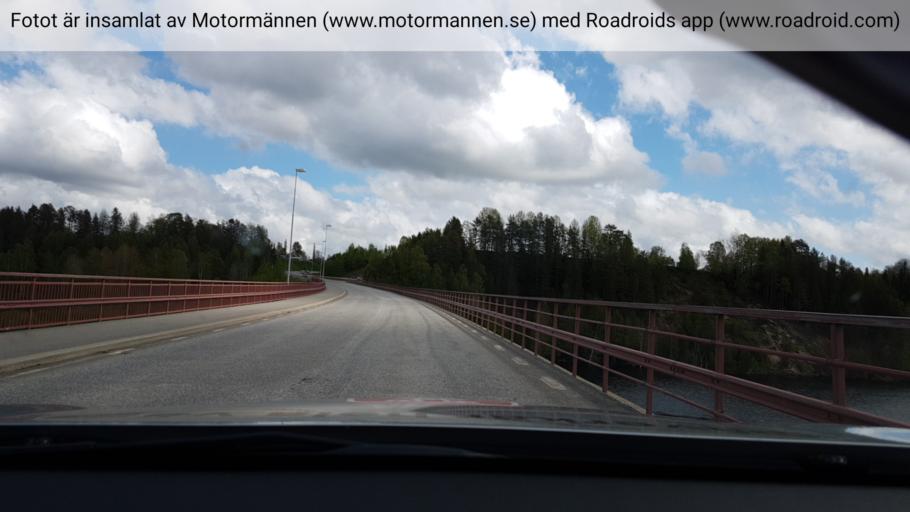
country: SE
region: Vaesterbotten
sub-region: Vindelns Kommun
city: Vindeln
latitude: 64.2000
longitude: 19.6978
